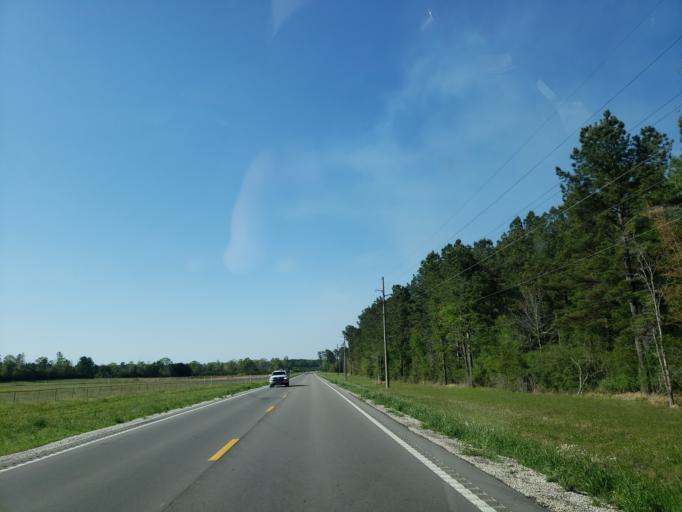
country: US
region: Mississippi
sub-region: Perry County
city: Richton
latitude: 31.3195
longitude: -88.9325
